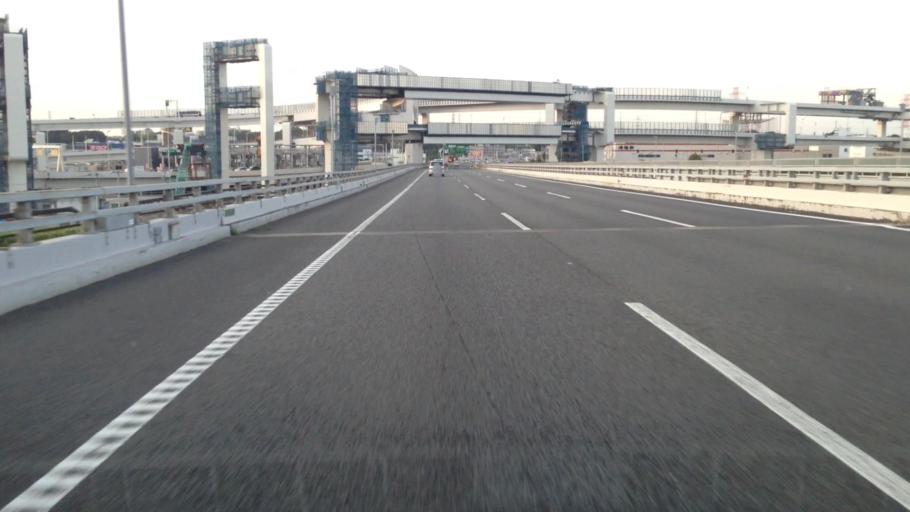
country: JP
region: Kanagawa
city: Yokohama
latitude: 35.5140
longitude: 139.5929
